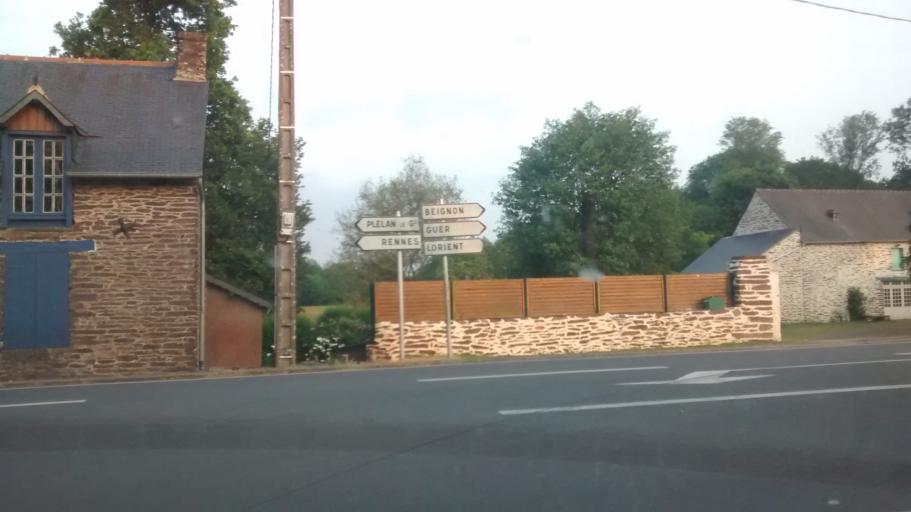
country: FR
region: Brittany
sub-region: Departement du Morbihan
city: Beignon
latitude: 47.9827
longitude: -2.1417
